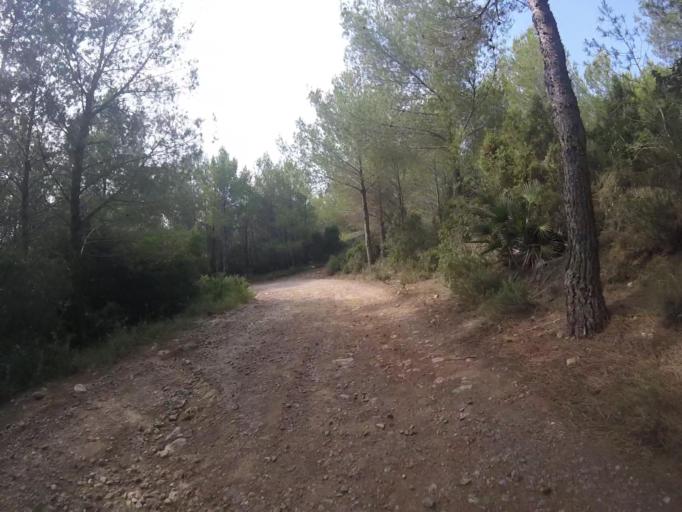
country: ES
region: Valencia
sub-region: Provincia de Castello
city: Benicassim
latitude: 40.0869
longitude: 0.0459
